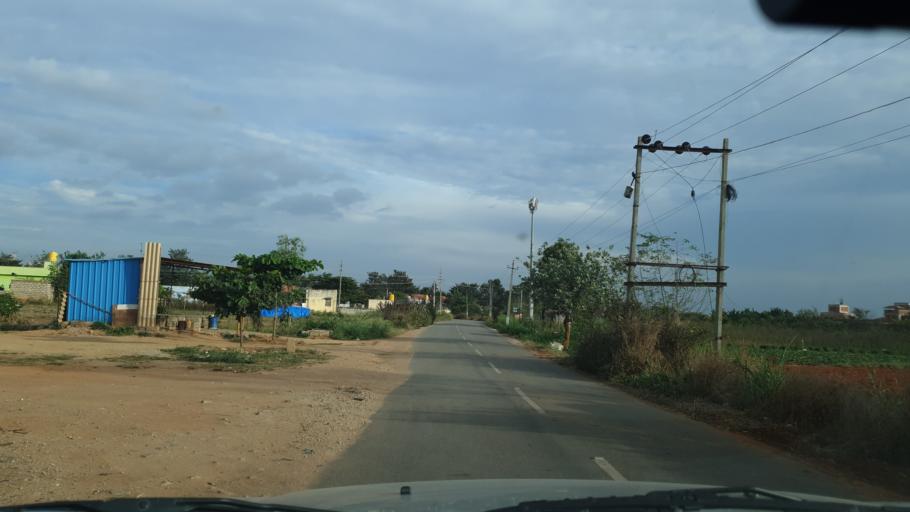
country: IN
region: Karnataka
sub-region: Bangalore Urban
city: Yelahanka
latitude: 13.1946
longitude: 77.6213
